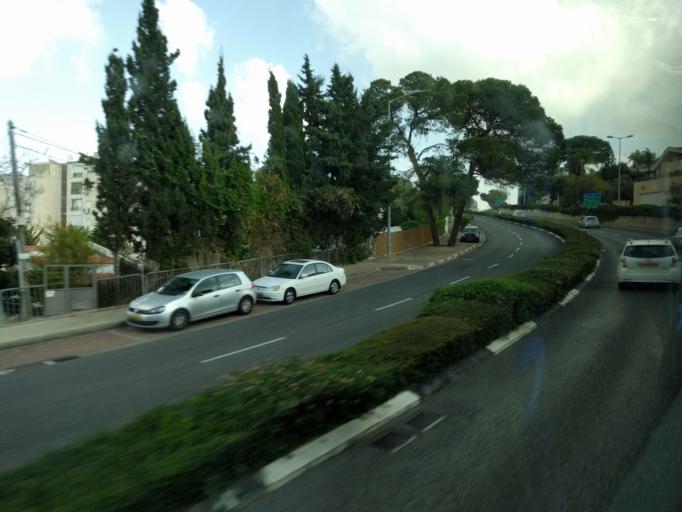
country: IL
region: Haifa
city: Nesher
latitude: 32.7685
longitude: 35.0079
